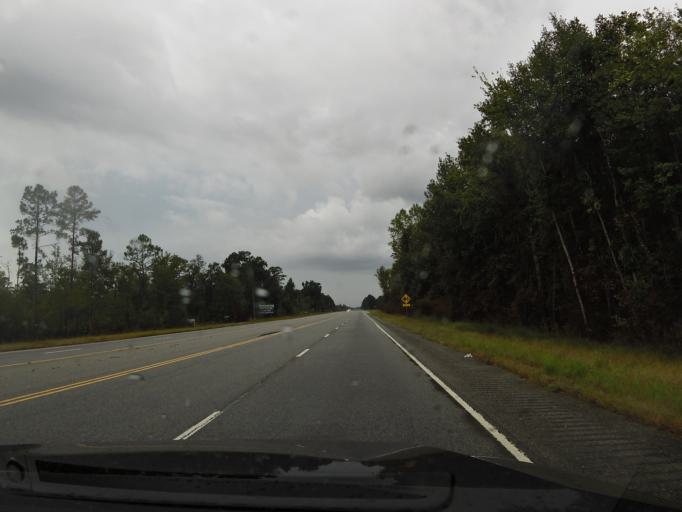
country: US
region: Georgia
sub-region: Wayne County
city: Jesup
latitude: 31.5354
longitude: -81.7952
